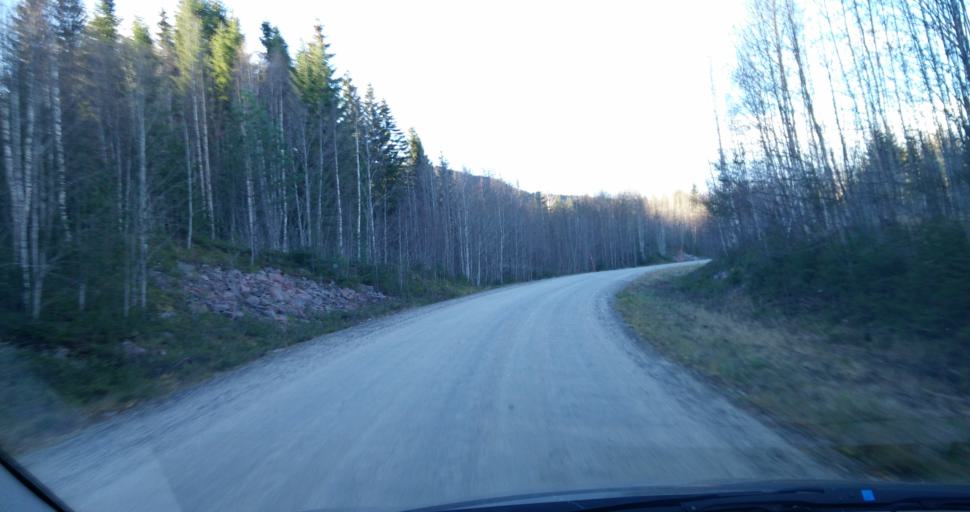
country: SE
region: Gaevleborg
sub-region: Nordanstigs Kommun
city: Bergsjoe
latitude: 62.0574
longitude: 16.7848
